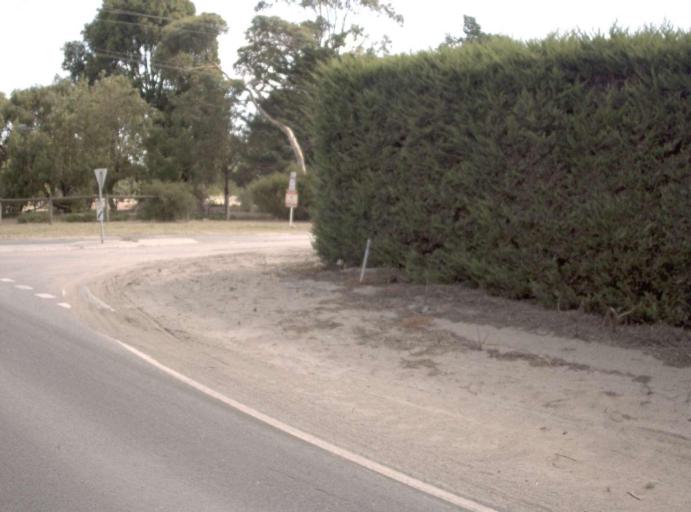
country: AU
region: Victoria
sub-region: Casey
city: Junction Village
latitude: -38.1333
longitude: 145.3243
